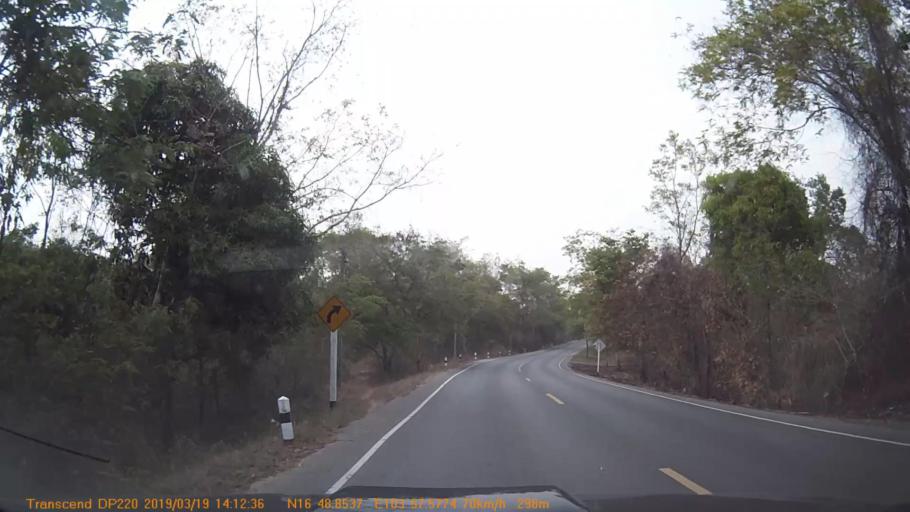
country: TH
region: Kalasin
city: Na Khu
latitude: 16.8146
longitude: 103.9594
